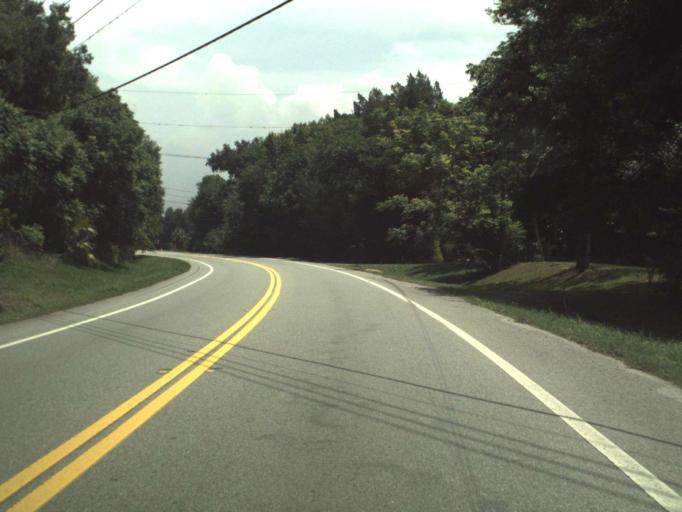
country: US
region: Florida
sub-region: Sumter County
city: Wildwood
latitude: 28.8015
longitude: -82.0464
